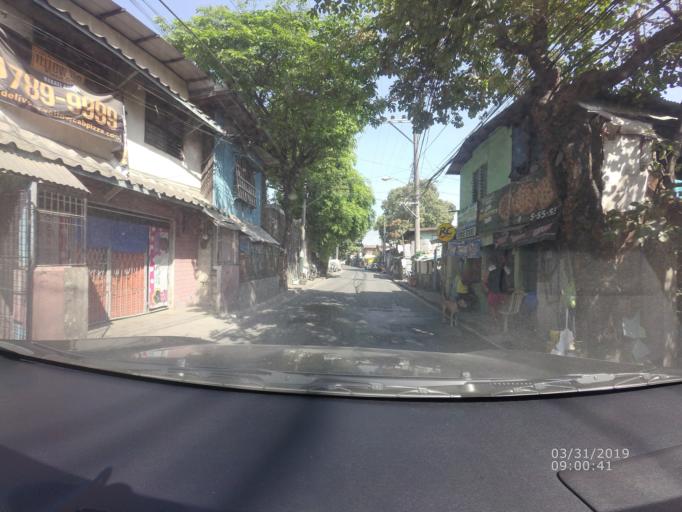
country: PH
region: Metro Manila
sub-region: Mandaluyong
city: Mandaluyong City
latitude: 14.5757
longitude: 121.0251
